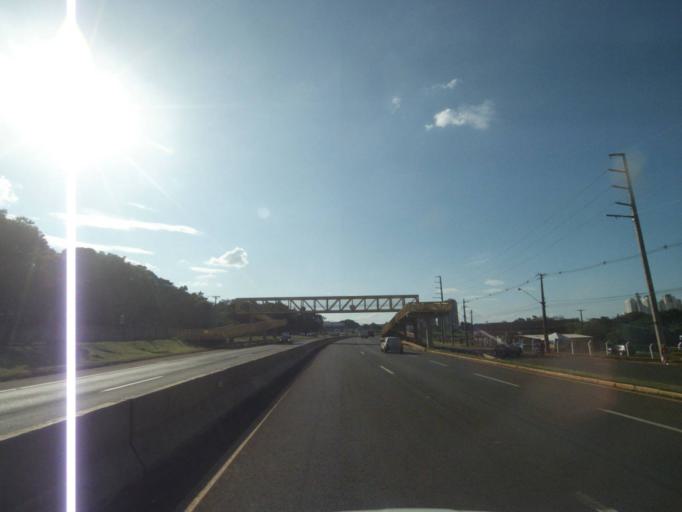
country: BR
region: Parana
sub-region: Londrina
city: Londrina
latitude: -23.3449
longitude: -51.1770
